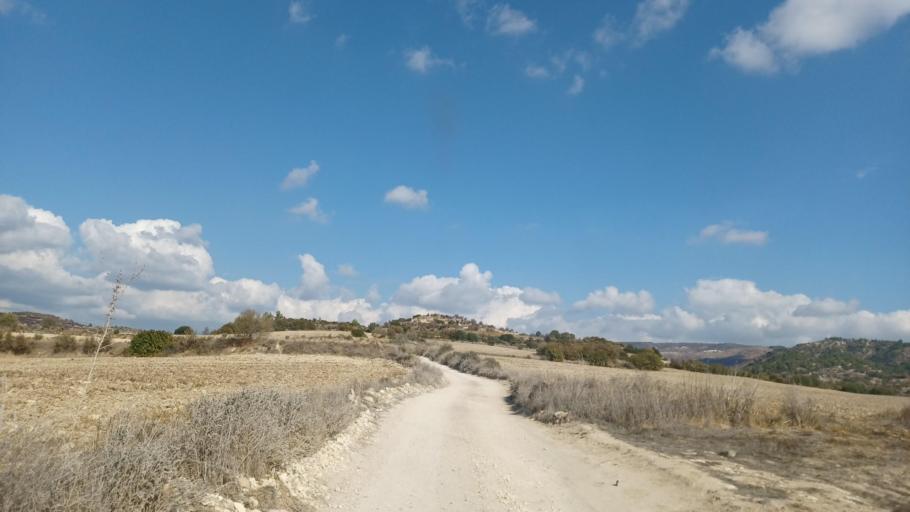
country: CY
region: Pafos
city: Mesogi
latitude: 34.8379
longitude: 32.5676
